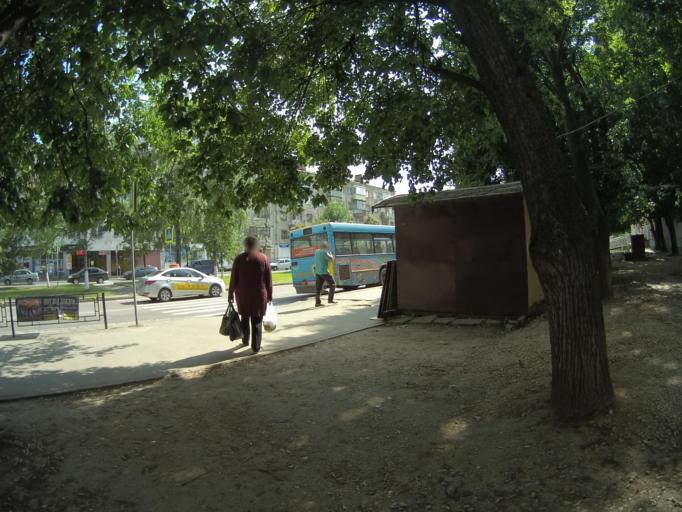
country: RU
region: Vladimir
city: Vladimir
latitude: 56.1406
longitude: 40.4044
